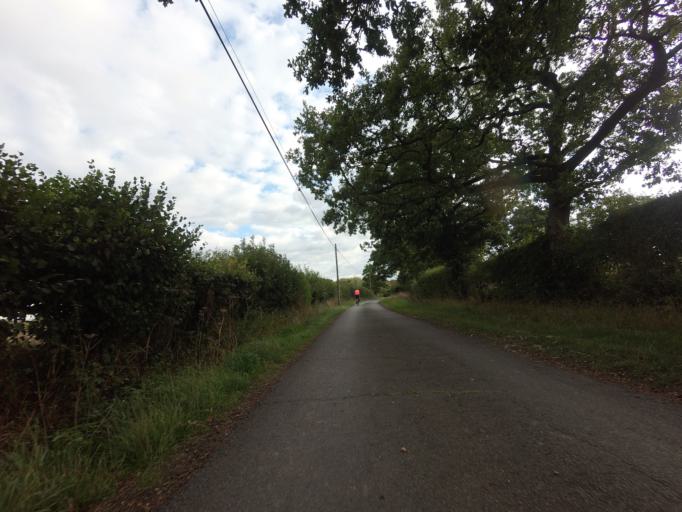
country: GB
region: England
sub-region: Kent
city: Staplehurst
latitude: 51.2006
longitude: 0.5690
